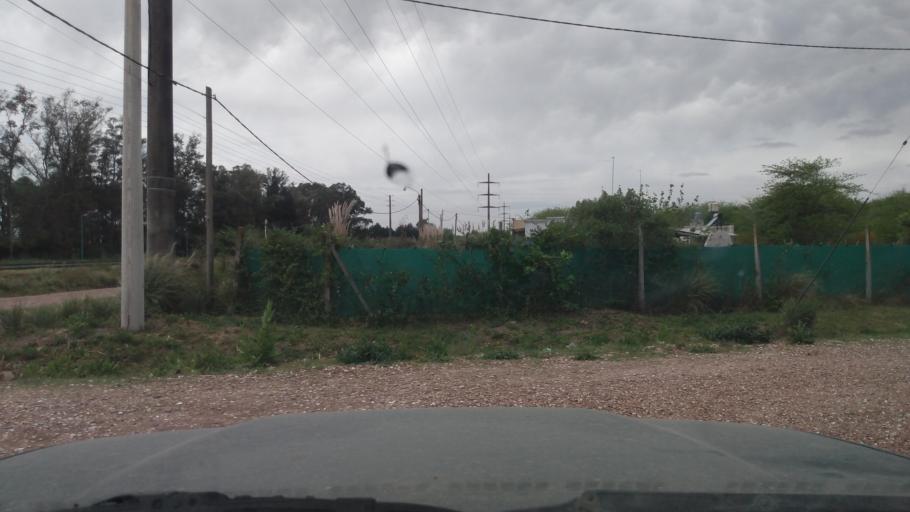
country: AR
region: Buenos Aires
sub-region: Partido de Lujan
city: Lujan
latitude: -34.5871
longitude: -59.1319
